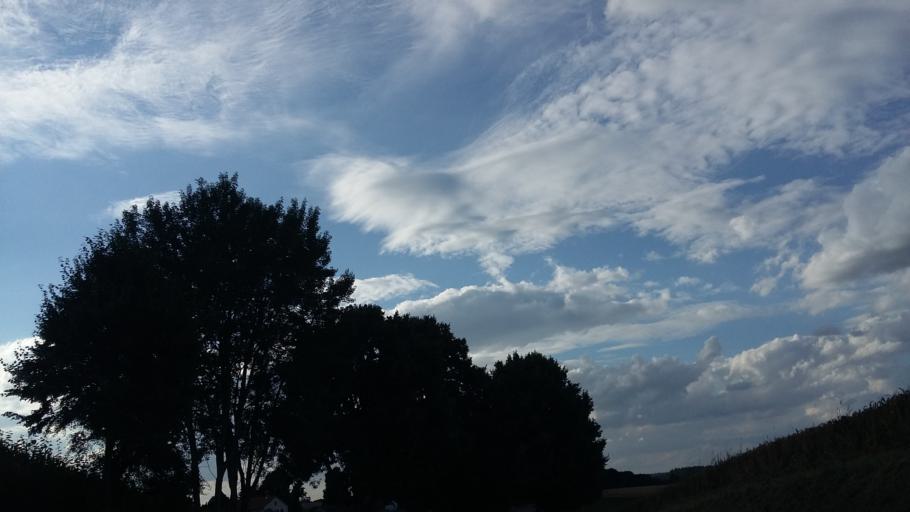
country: DE
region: Bavaria
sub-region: Upper Bavaria
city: Mittelstetten
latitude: 48.2442
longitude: 11.1008
